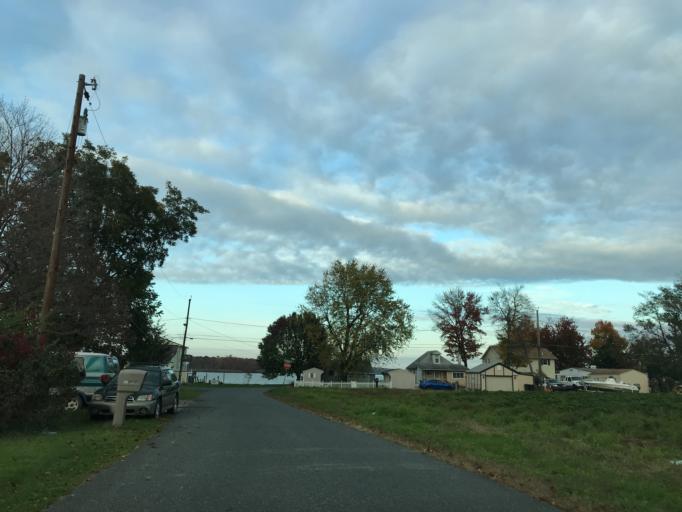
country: US
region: Maryland
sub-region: Baltimore County
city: Bowleys Quarters
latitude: 39.3735
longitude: -76.3765
